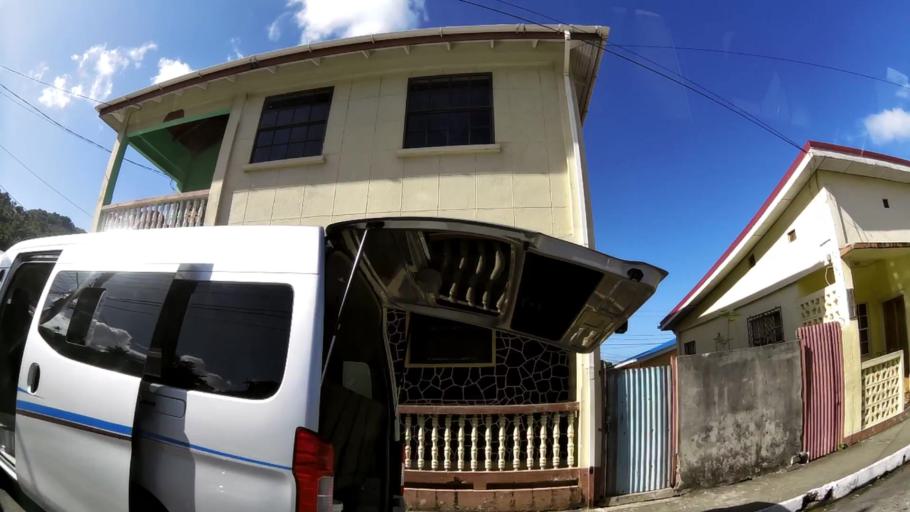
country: LC
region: Soufriere
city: Soufriere
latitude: 13.8546
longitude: -61.0578
